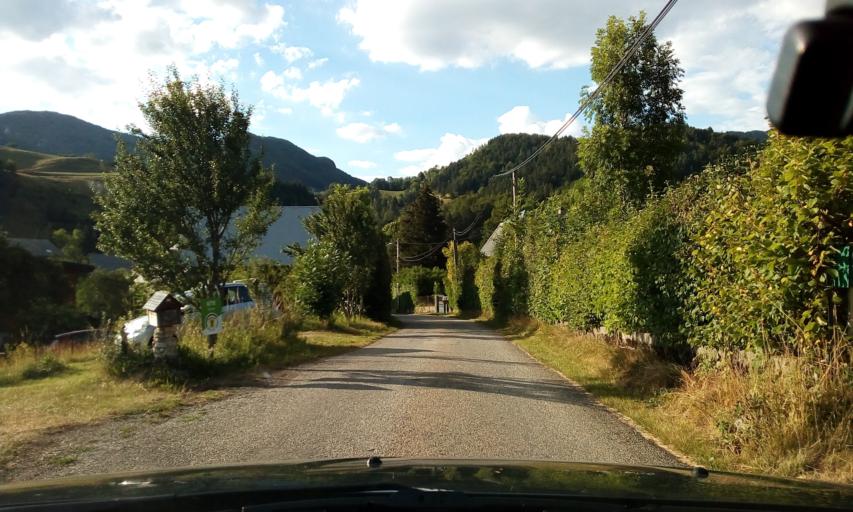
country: FR
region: Rhone-Alpes
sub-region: Departement de l'Isere
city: Barraux
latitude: 45.4580
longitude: 5.8905
